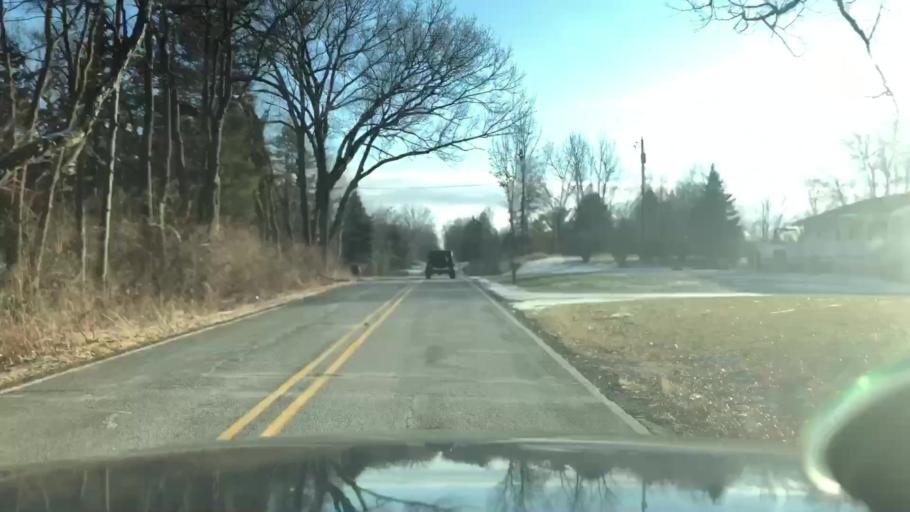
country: US
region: Michigan
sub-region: Jackson County
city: Vandercook Lake
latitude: 42.1389
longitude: -84.4517
